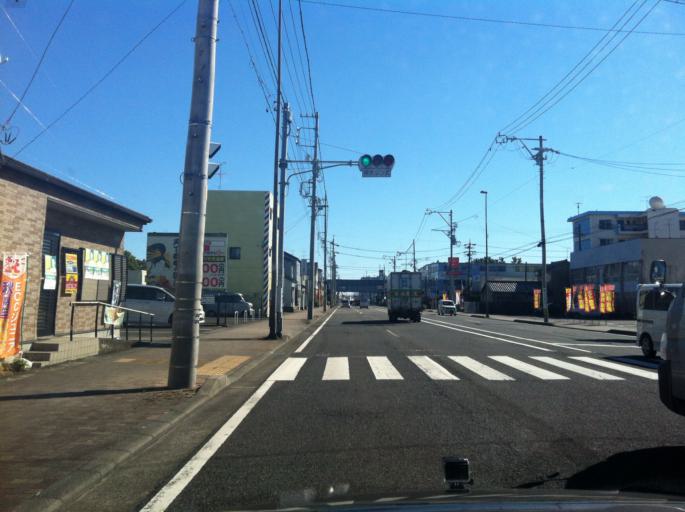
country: JP
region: Shizuoka
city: Shizuoka-shi
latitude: 34.9540
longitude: 138.4058
